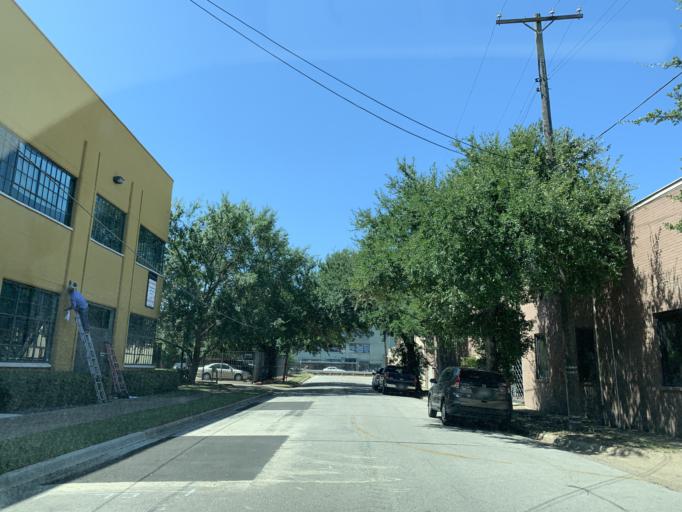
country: US
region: Texas
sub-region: Dallas County
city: Dallas
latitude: 32.7861
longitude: -96.7705
